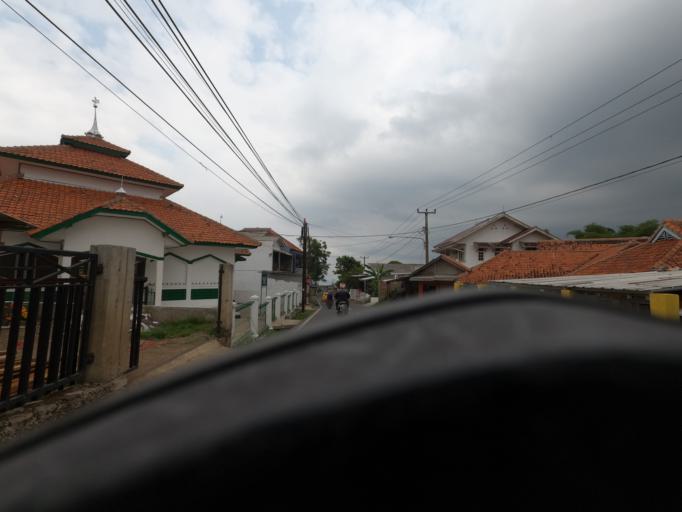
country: ID
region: West Java
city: Cimahi
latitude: -6.8226
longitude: 107.5333
